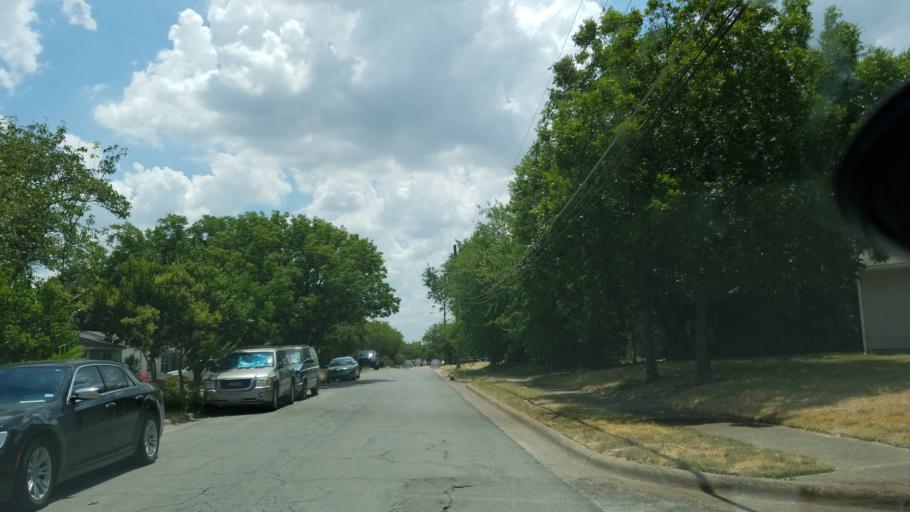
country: US
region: Texas
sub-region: Dallas County
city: Cockrell Hill
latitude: 32.7173
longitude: -96.8939
